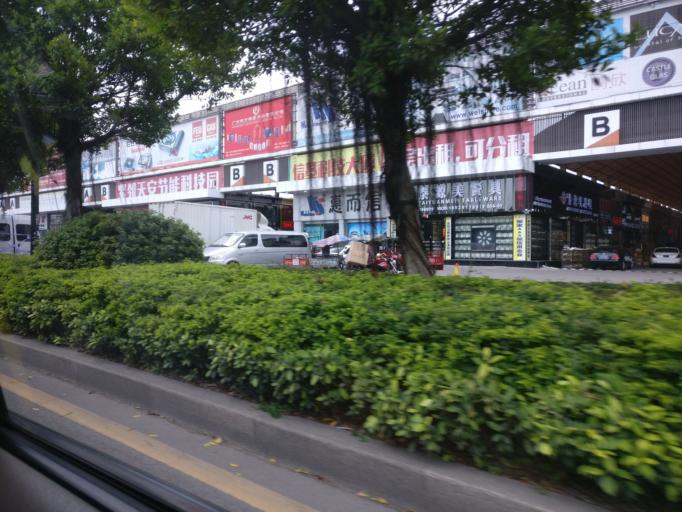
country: CN
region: Guangdong
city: Dashi
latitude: 23.0376
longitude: 113.3285
